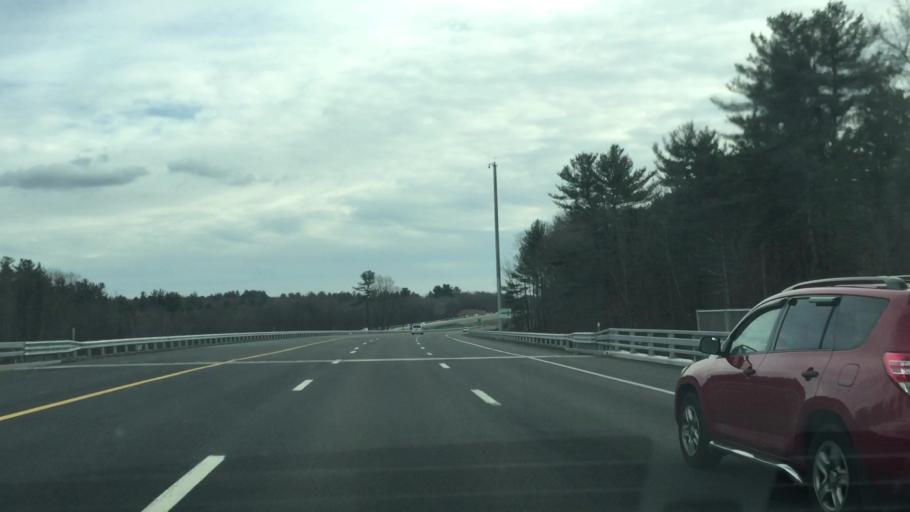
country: US
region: New Hampshire
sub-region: Rockingham County
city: Derry
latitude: 42.8551
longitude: -71.3188
